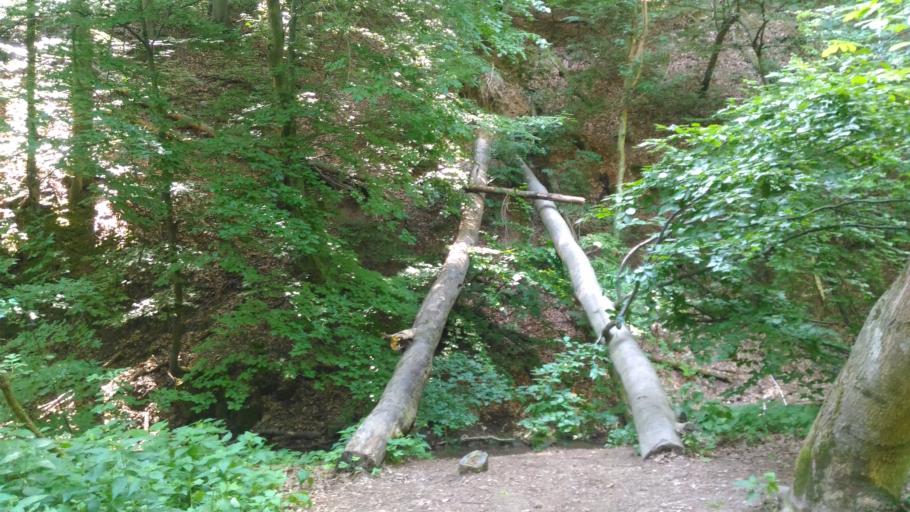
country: HU
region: Baranya
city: Pecsvarad
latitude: 46.2146
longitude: 18.3908
